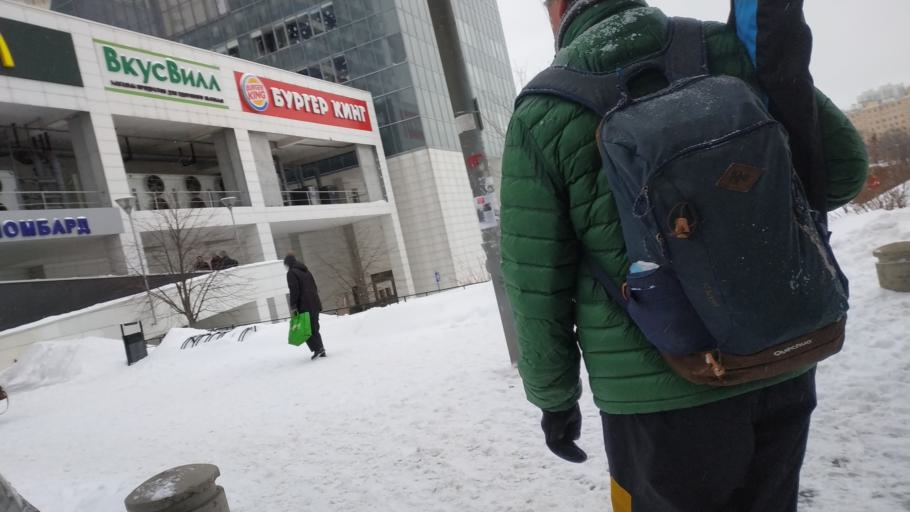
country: RU
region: Moscow
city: Nagornyy
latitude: 55.6364
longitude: 37.5981
